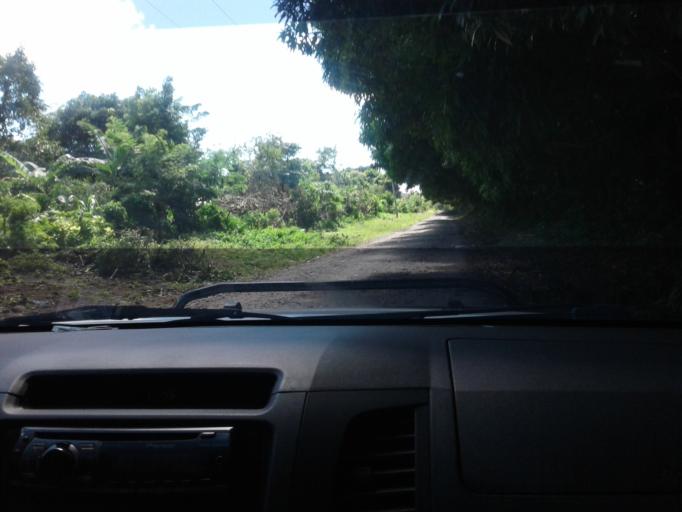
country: NI
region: Rivas
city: Altagracia
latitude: 11.4636
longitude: -85.5601
